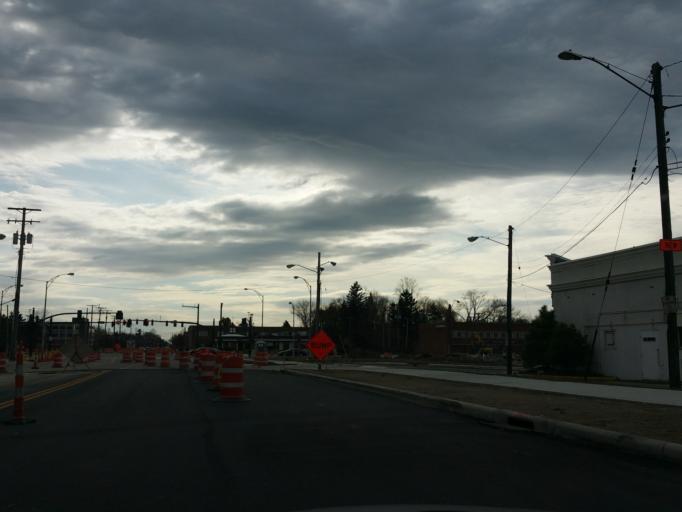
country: US
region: Ohio
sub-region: Cuyahoga County
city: Shaker Heights
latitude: 41.4658
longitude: -81.5363
